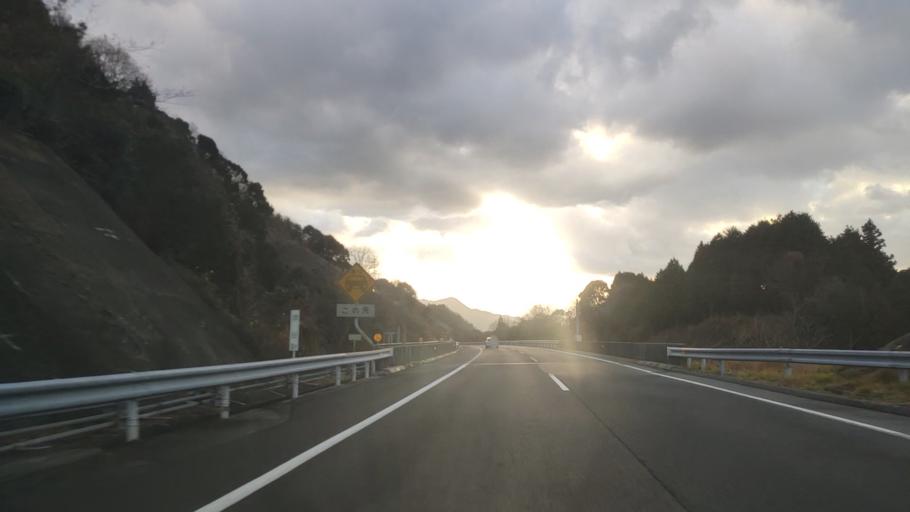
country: JP
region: Ehime
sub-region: Shikoku-chuo Shi
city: Matsuyama
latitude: 33.8177
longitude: 132.9599
